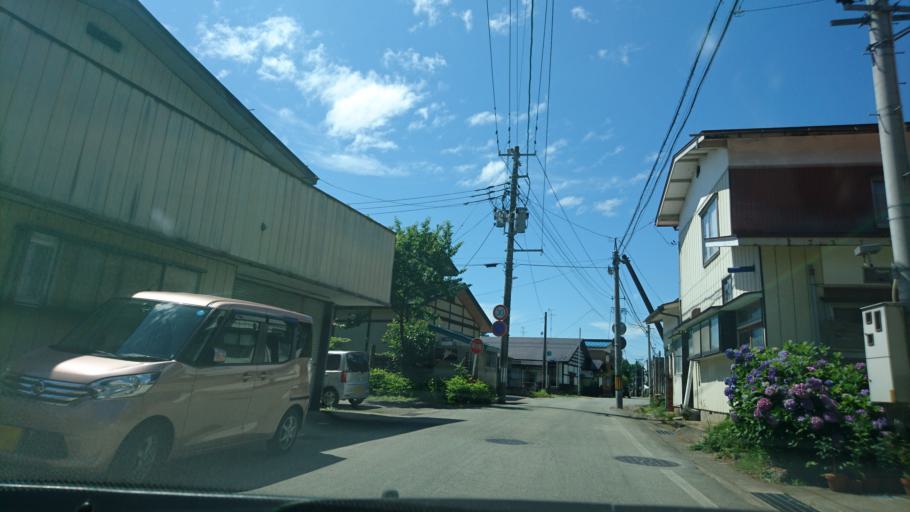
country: JP
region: Akita
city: Kakunodatemachi
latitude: 39.5876
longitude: 140.5643
